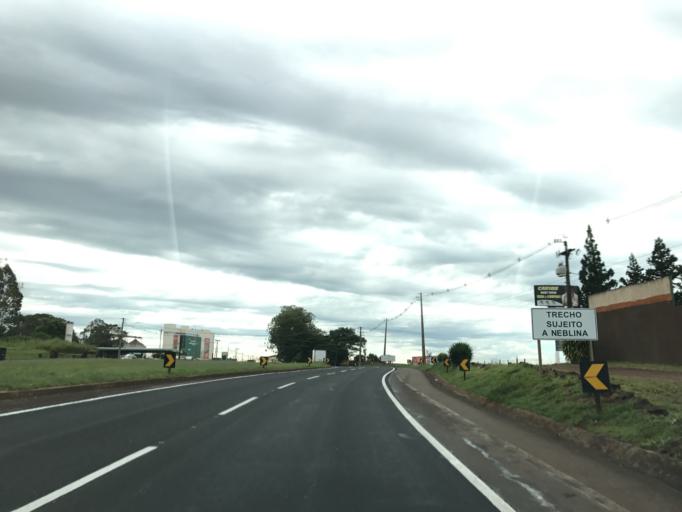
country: BR
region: Parana
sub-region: Rolandia
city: Rolandia
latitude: -23.3586
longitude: -51.3966
